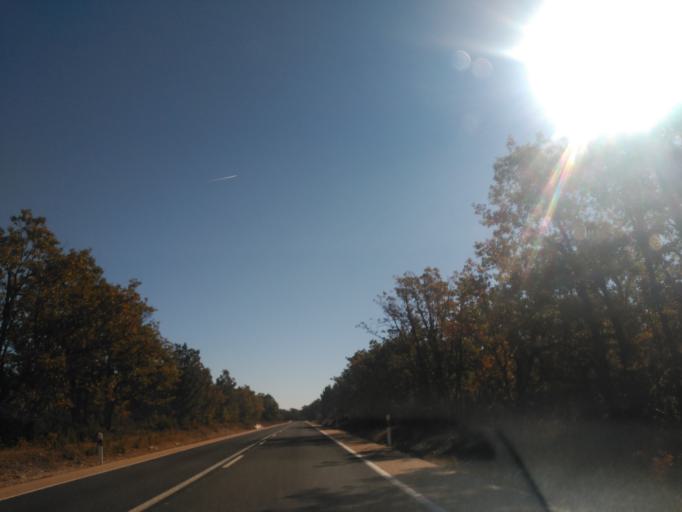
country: ES
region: Castille and Leon
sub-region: Provincia de Soria
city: Cidones
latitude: 41.8104
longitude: -2.6930
